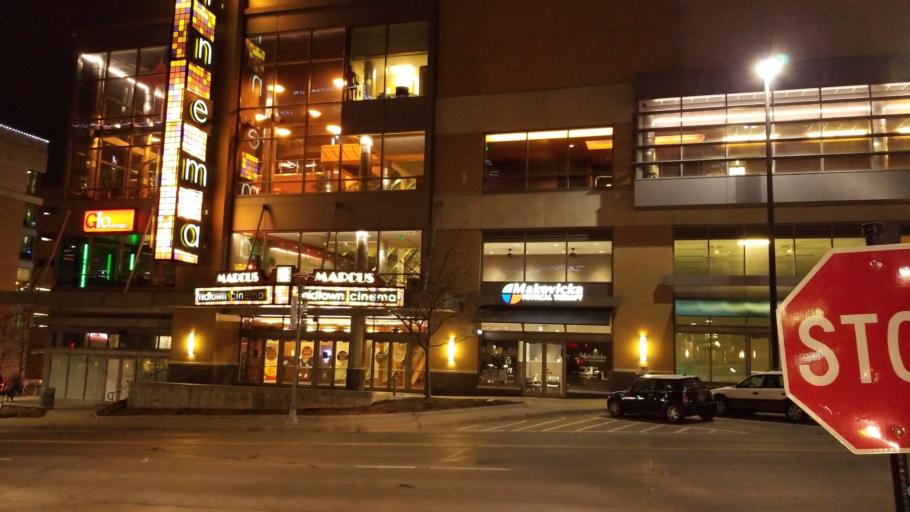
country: US
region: Nebraska
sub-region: Douglas County
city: Omaha
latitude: 41.2578
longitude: -95.9604
